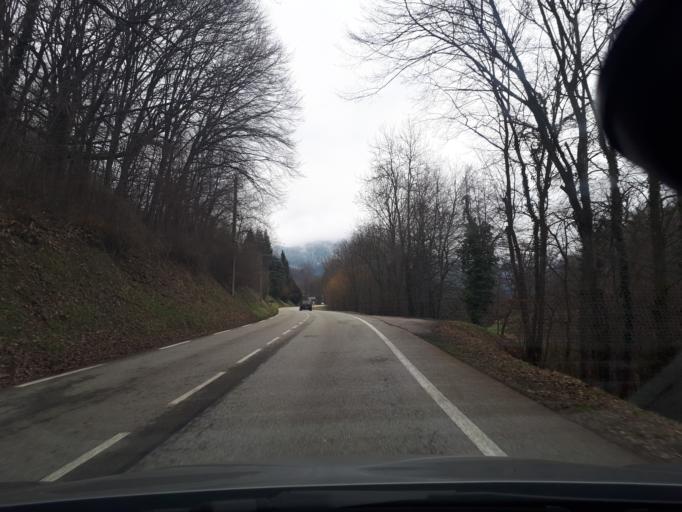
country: FR
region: Rhone-Alpes
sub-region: Departement de l'Isere
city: Vaulnaveys-le-Haut
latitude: 45.1257
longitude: 5.8271
